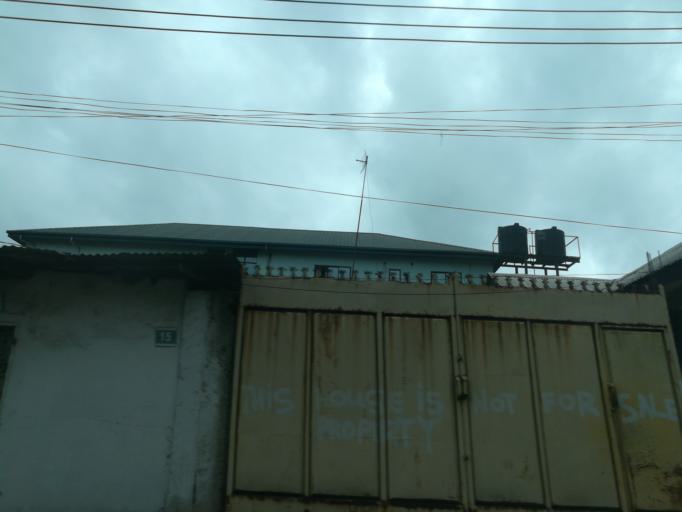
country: NG
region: Rivers
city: Port Harcourt
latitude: 4.8403
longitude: 7.0362
